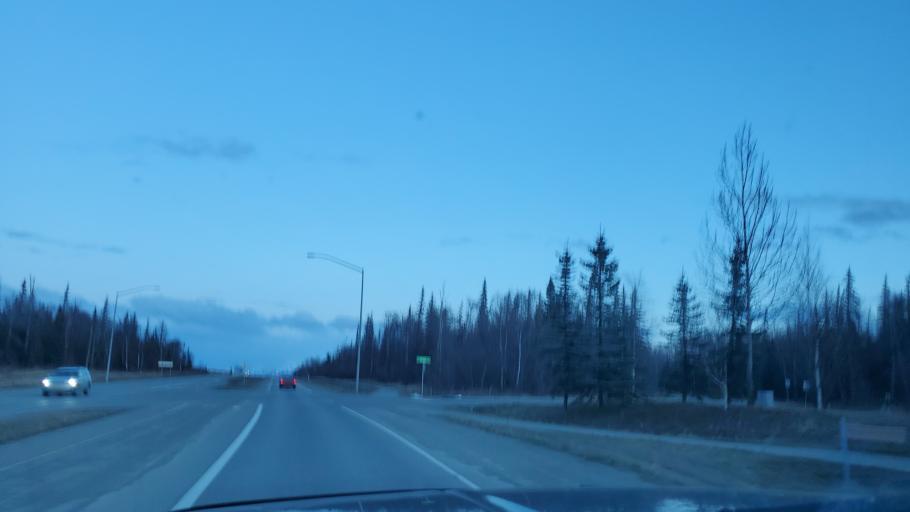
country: US
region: Alaska
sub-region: Matanuska-Susitna Borough
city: Wasilla
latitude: 61.5707
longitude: -149.4357
